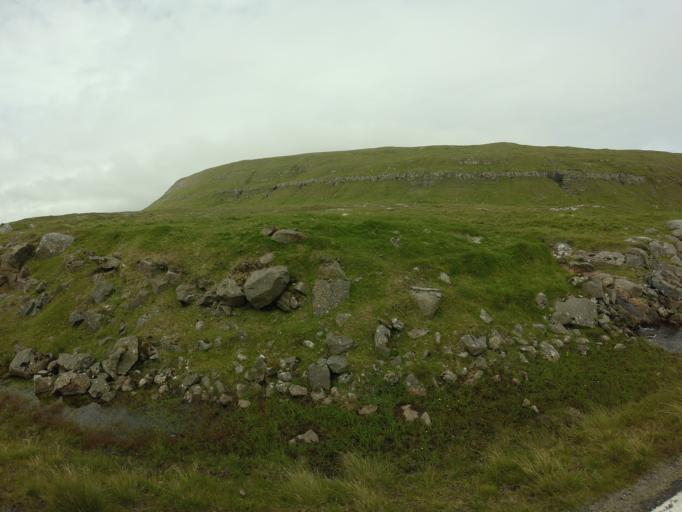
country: FO
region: Sandoy
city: Sandur
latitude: 61.8230
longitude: -6.7296
